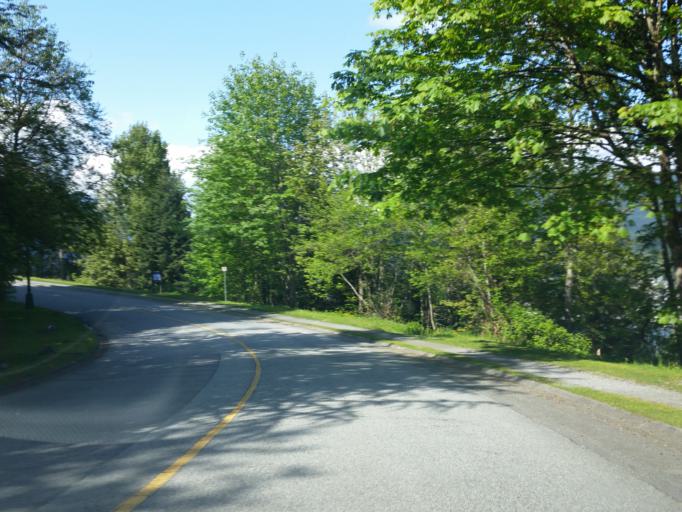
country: CA
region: British Columbia
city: Port Moody
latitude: 49.2856
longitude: -122.8709
